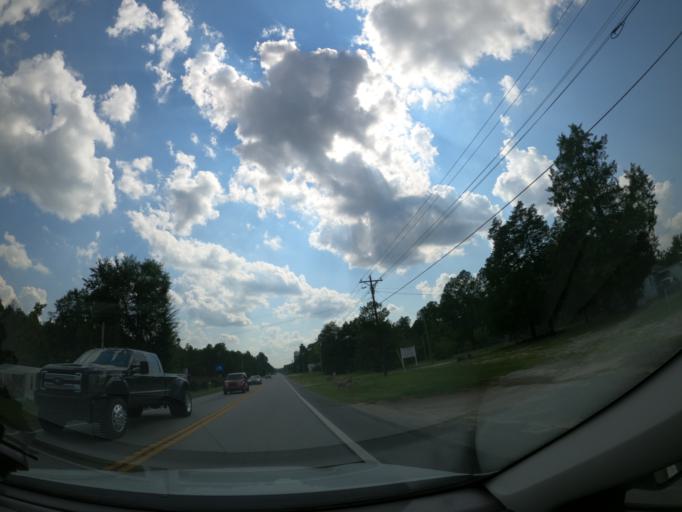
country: US
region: South Carolina
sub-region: Lexington County
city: South Congaree
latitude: 33.8712
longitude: -81.1887
